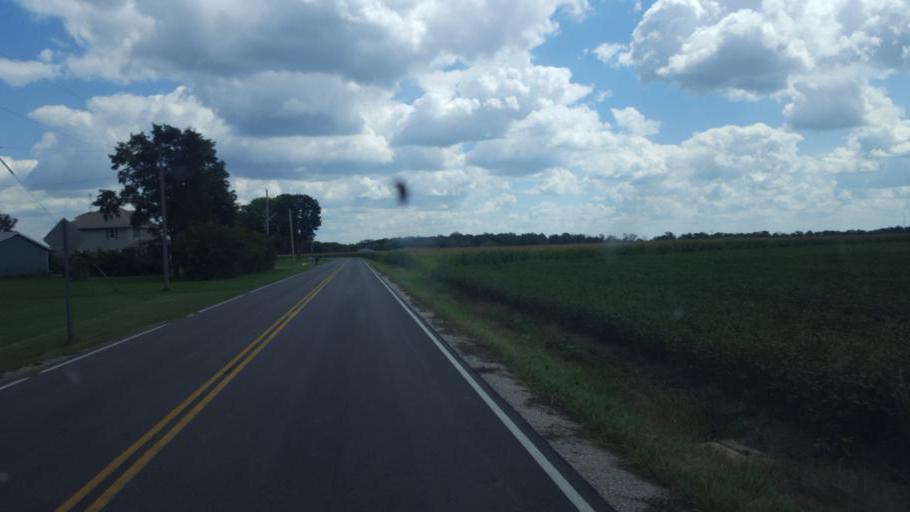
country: US
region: Ohio
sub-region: Ottawa County
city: Elmore
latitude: 41.4651
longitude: -83.3168
